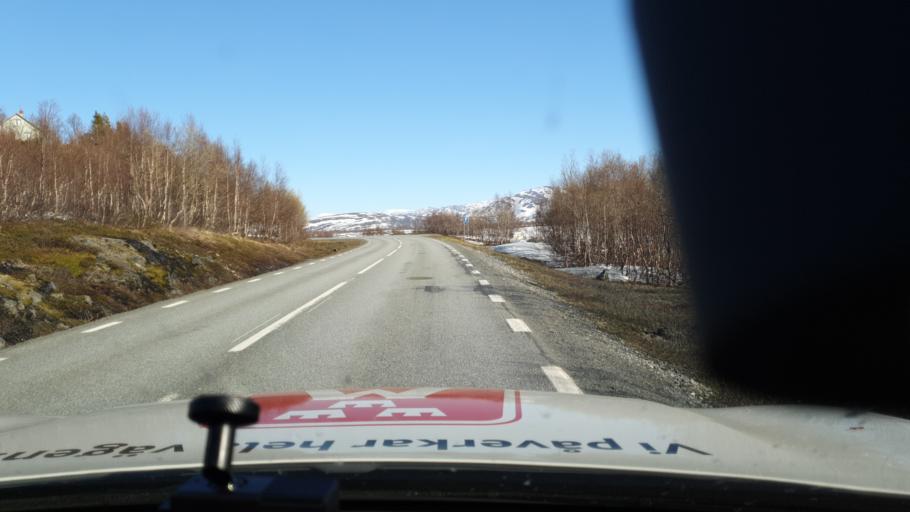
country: NO
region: Nordland
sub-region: Rana
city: Mo i Rana
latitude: 66.1254
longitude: 14.6620
